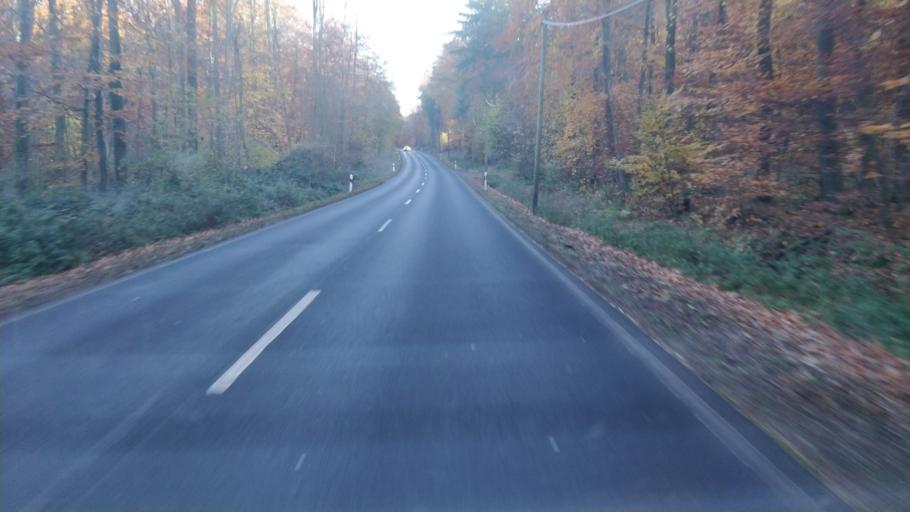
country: DE
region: North Rhine-Westphalia
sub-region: Regierungsbezirk Koln
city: Rheinbach
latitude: 50.6152
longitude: 6.9179
